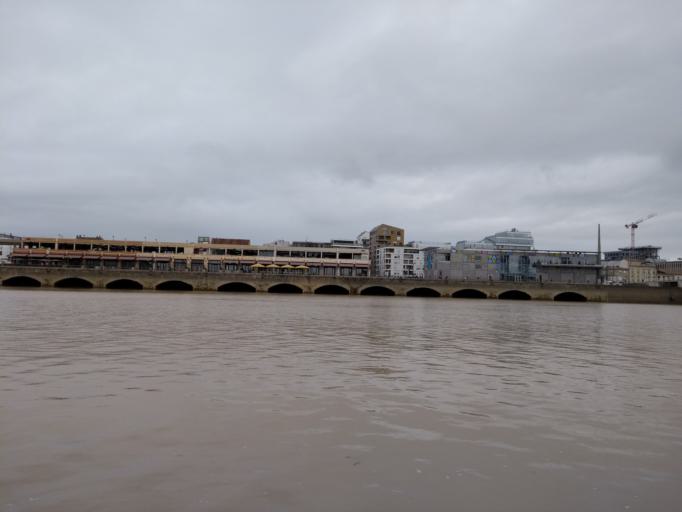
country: FR
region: Aquitaine
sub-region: Departement de la Gironde
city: Bordeaux
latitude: 44.8576
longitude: -0.5537
